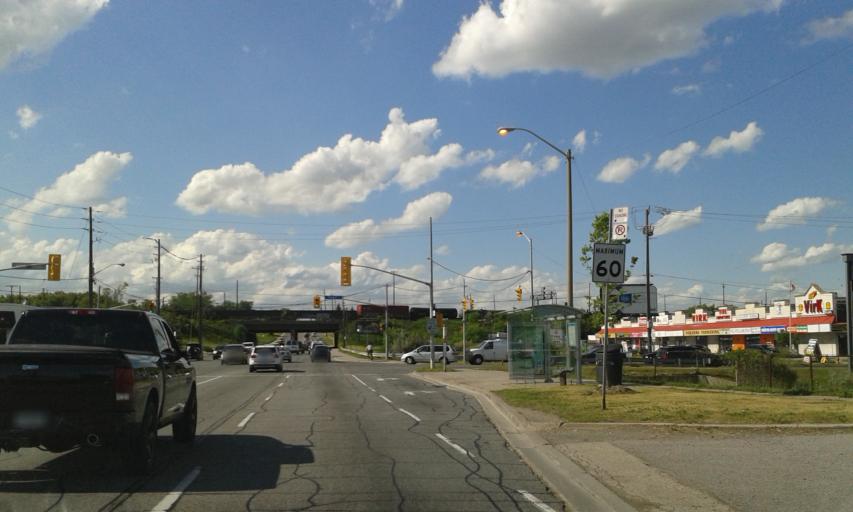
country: CA
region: Ontario
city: Scarborough
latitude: 43.7913
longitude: -79.2594
